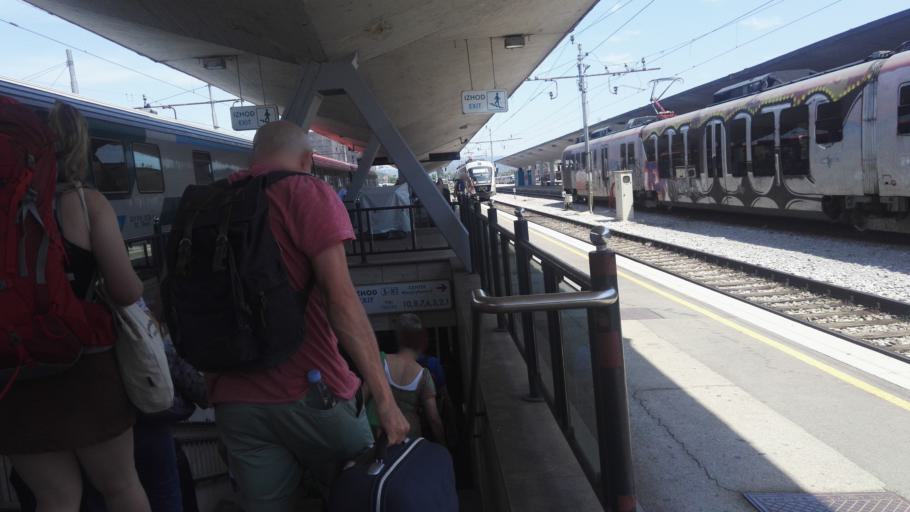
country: SI
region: Ljubljana
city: Ljubljana
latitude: 46.0589
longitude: 14.5128
